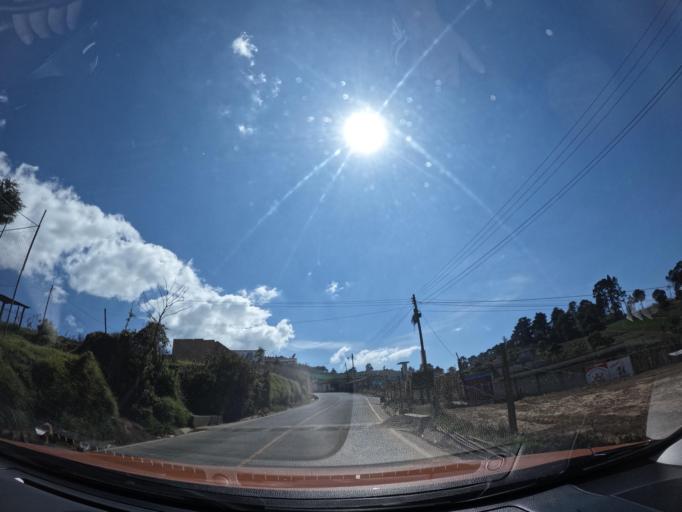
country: GT
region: Chimaltenango
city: Patzun
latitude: 14.6558
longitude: -91.0548
